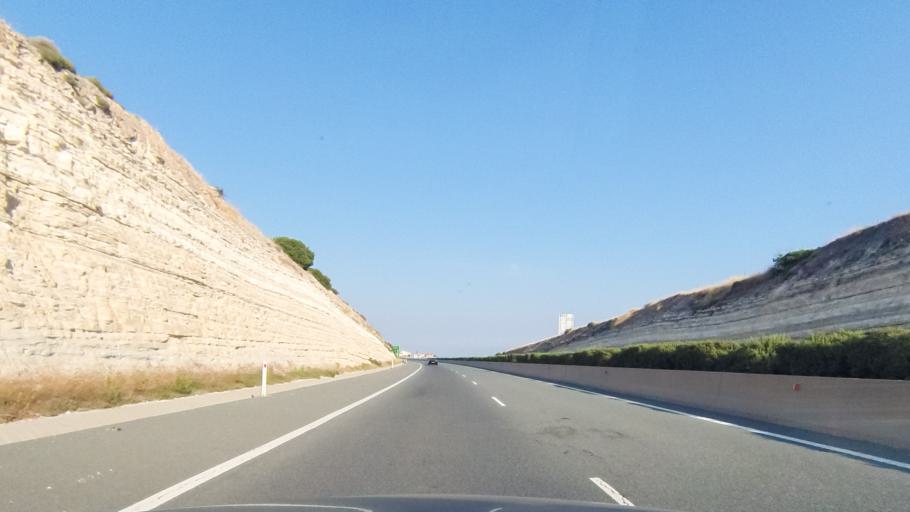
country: CY
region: Limassol
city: Sotira
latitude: 34.6853
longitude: 32.8773
